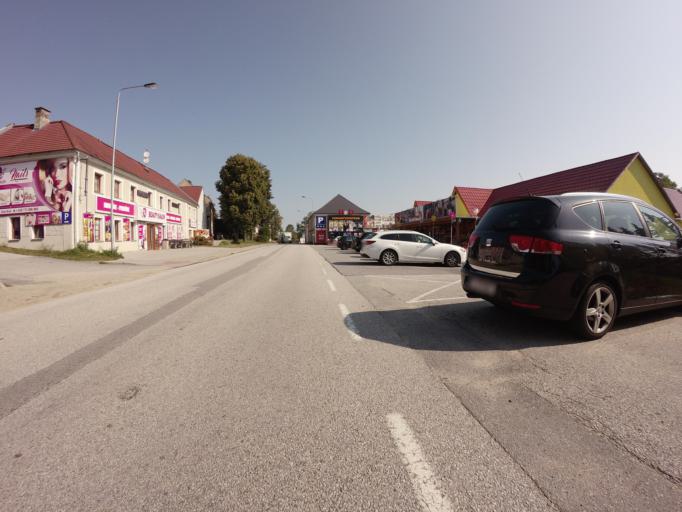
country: CZ
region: Jihocesky
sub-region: Okres Cesky Krumlov
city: Vyssi Brod
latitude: 48.5892
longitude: 14.3259
